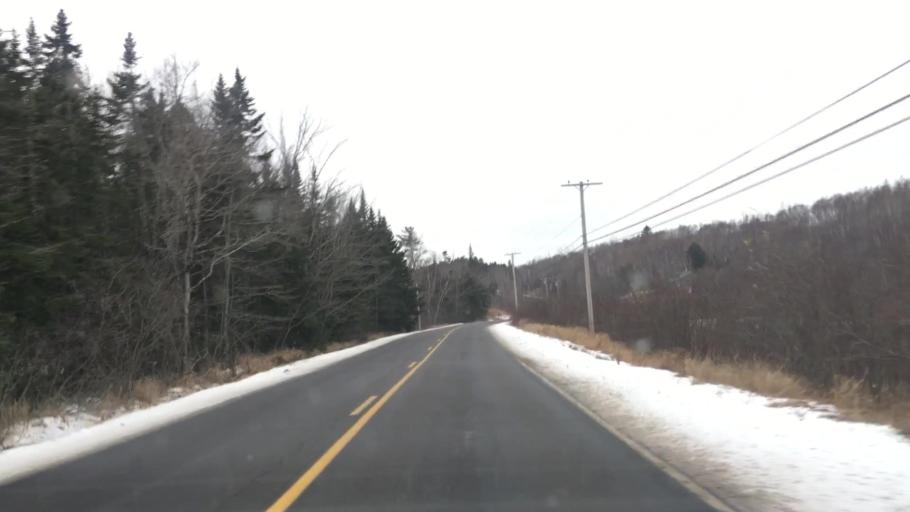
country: US
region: Maine
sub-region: Washington County
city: Machiasport
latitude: 44.7112
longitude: -67.3717
